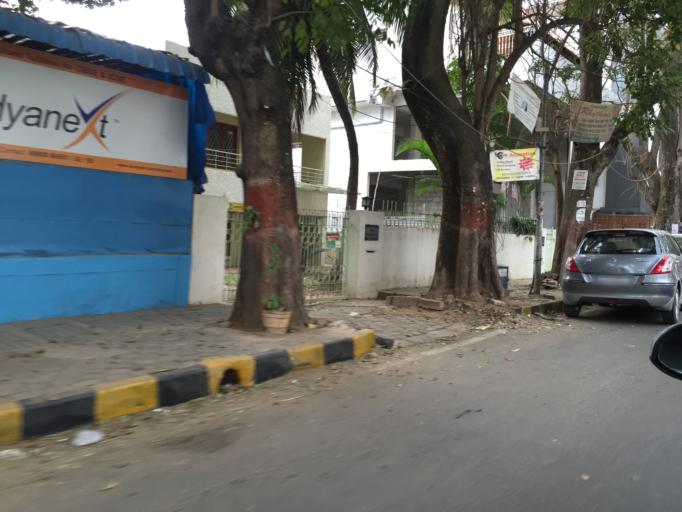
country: IN
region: Karnataka
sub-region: Bangalore Urban
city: Bangalore
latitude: 12.9764
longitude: 77.6363
